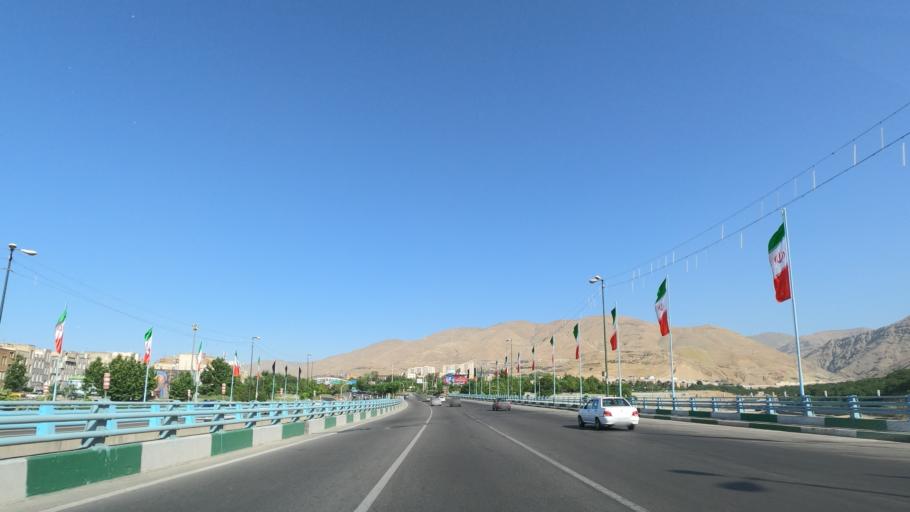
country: IR
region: Tehran
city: Shahr-e Qods
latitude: 35.7560
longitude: 51.2689
